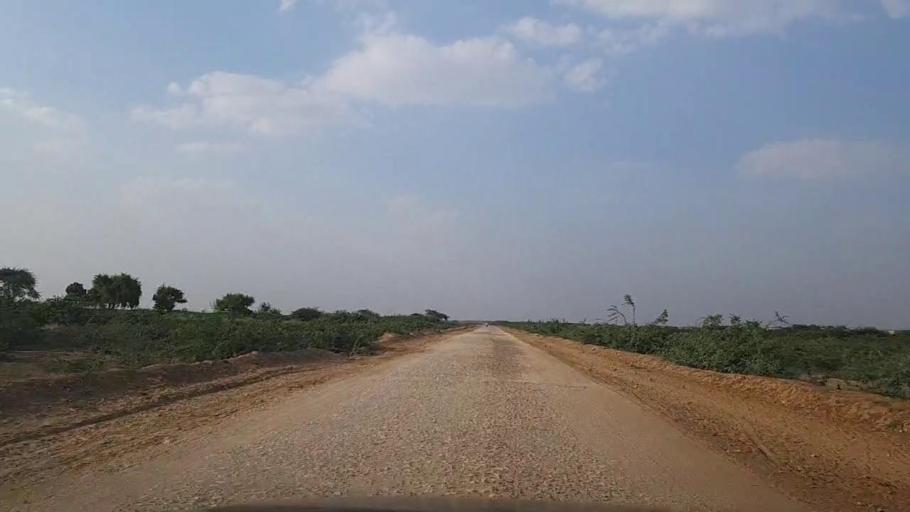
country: PK
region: Sindh
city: Gharo
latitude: 24.8009
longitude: 67.7434
